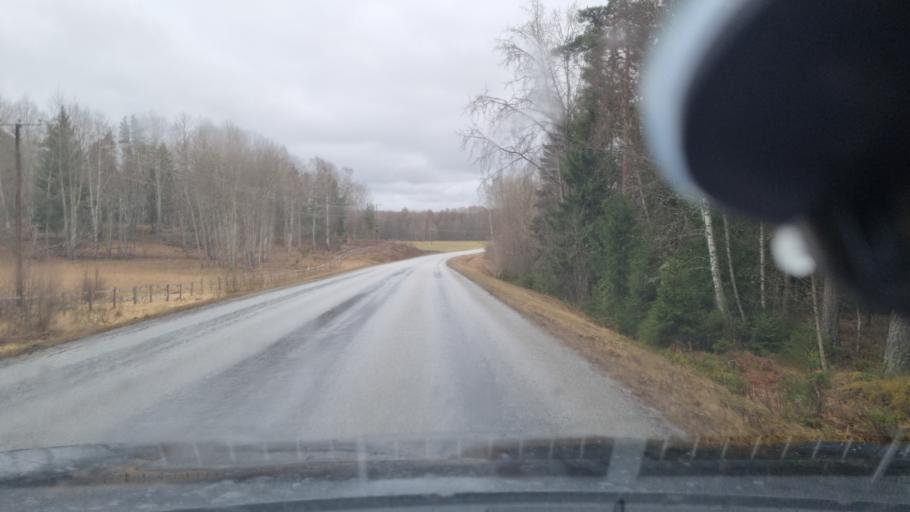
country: SE
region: Stockholm
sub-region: Sigtuna Kommun
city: Sigtuna
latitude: 59.5529
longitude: 17.7300
